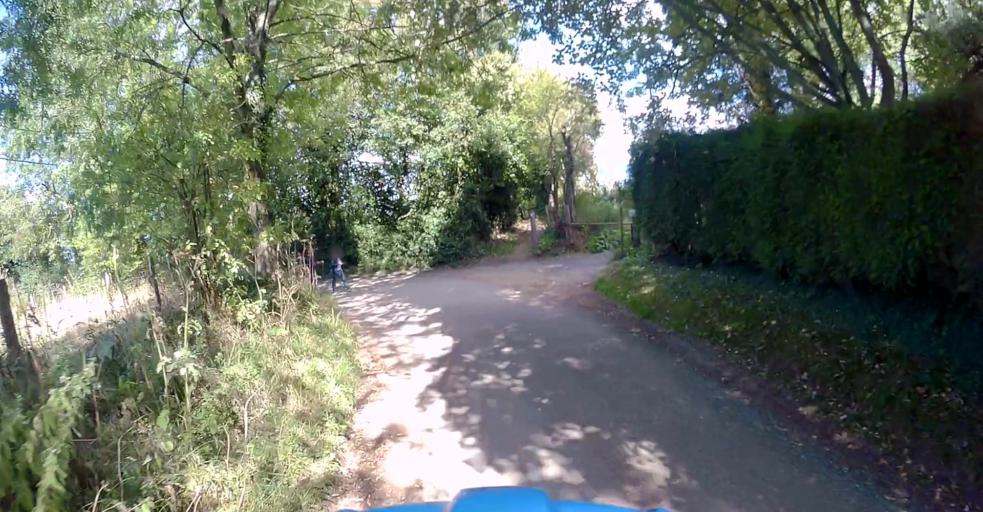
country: GB
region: England
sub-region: Hampshire
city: Four Marks
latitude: 51.1555
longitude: -1.0906
